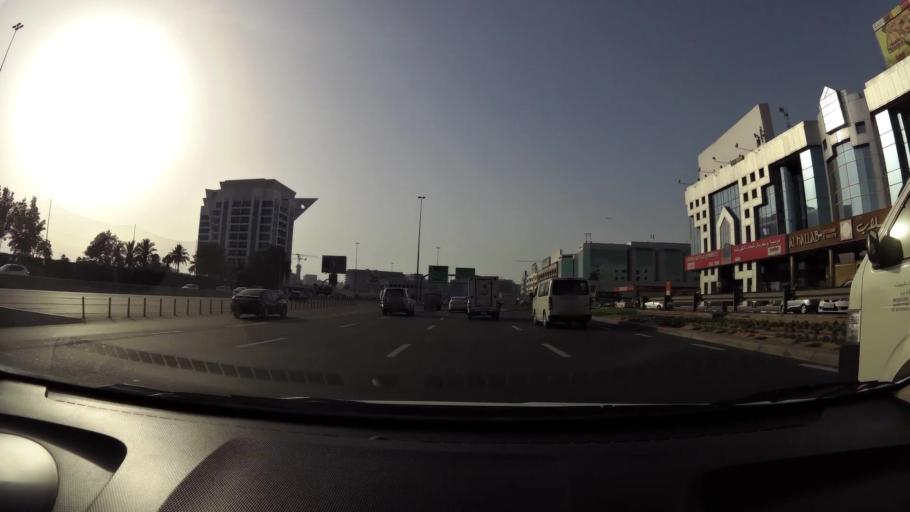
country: AE
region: Ash Shariqah
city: Sharjah
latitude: 25.2449
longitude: 55.3387
